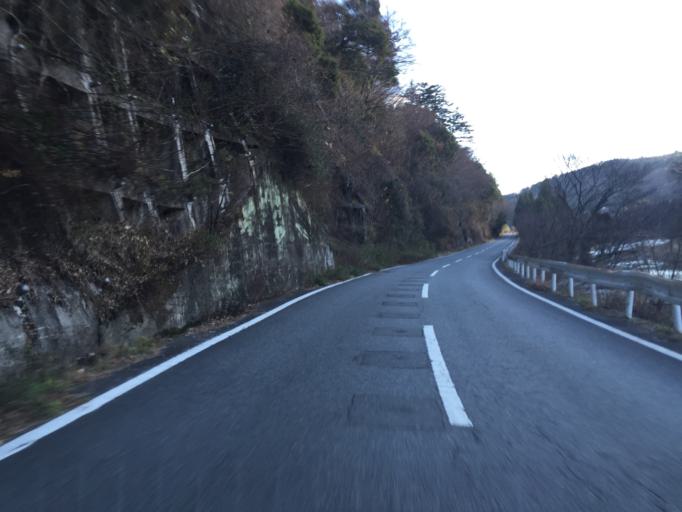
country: JP
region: Fukushima
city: Iwaki
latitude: 37.1522
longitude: 140.8314
